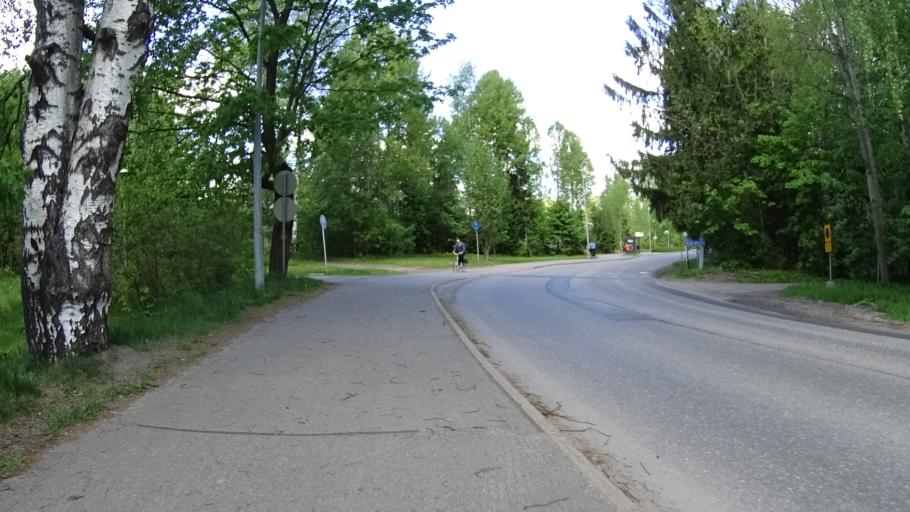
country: FI
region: Uusimaa
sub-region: Helsinki
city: Kauniainen
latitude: 60.2248
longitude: 24.7063
